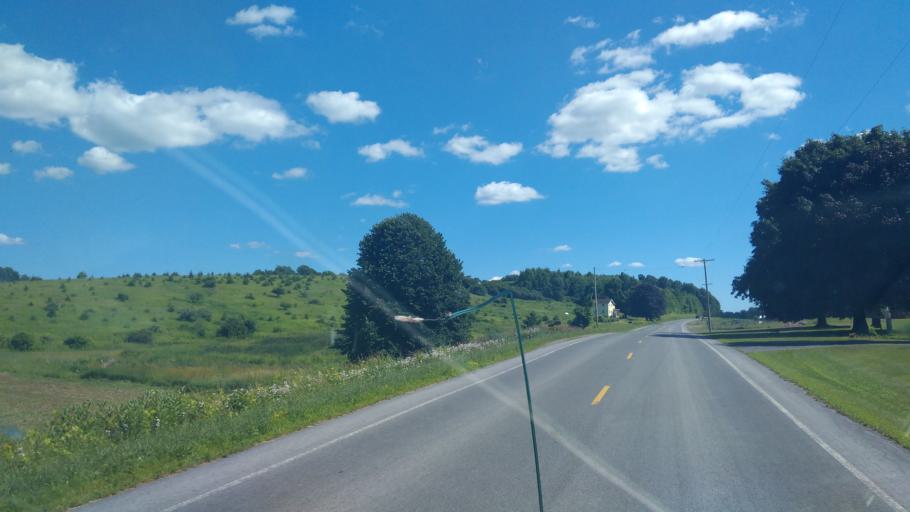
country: US
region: New York
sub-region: Wayne County
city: Lyons
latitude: 43.1129
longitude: -77.0093
